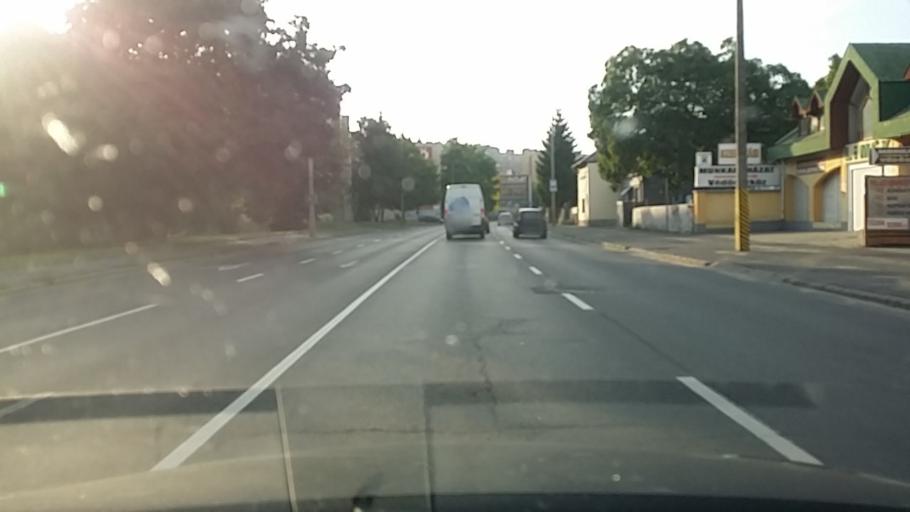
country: HU
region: Borsod-Abauj-Zemplen
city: Miskolc
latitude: 48.0739
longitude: 20.7876
